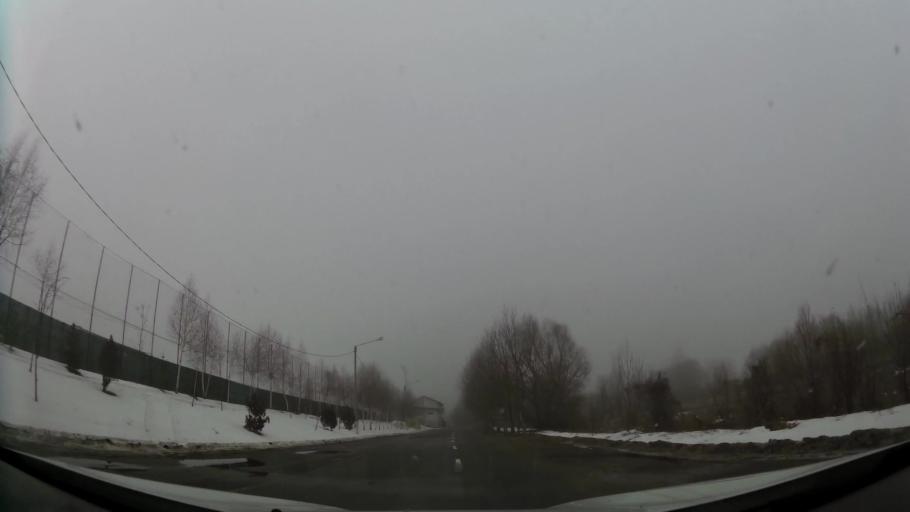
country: RO
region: Ilfov
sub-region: Comuna Chiajna
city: Chiajna
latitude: 44.4662
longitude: 25.9796
